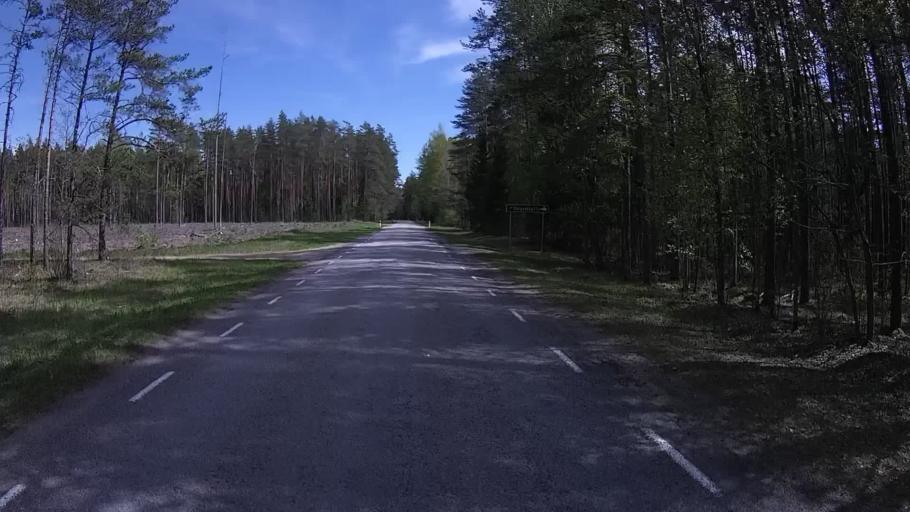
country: EE
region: Vorumaa
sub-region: Antsla vald
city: Vana-Antsla
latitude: 57.6118
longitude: 26.4257
